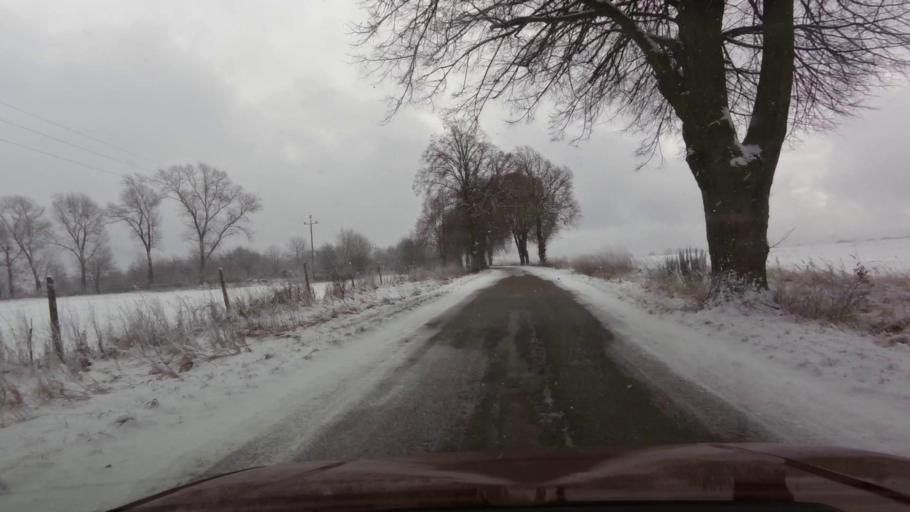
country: PL
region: West Pomeranian Voivodeship
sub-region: Powiat swidwinski
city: Rabino
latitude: 53.8755
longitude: 15.9376
